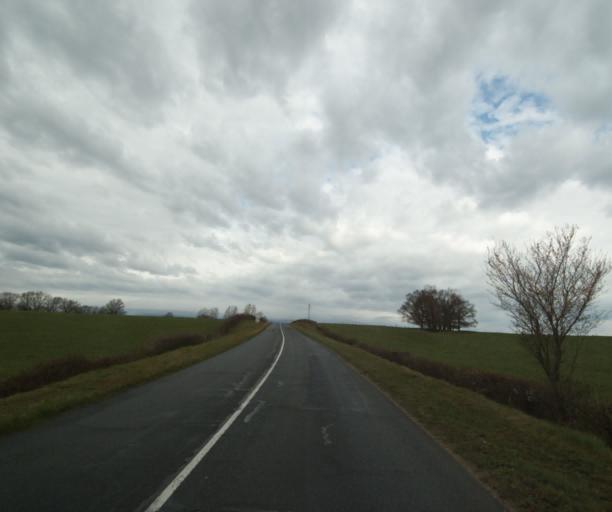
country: FR
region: Auvergne
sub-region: Departement de l'Allier
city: Toulon-sur-Allier
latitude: 46.5016
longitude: 3.3783
